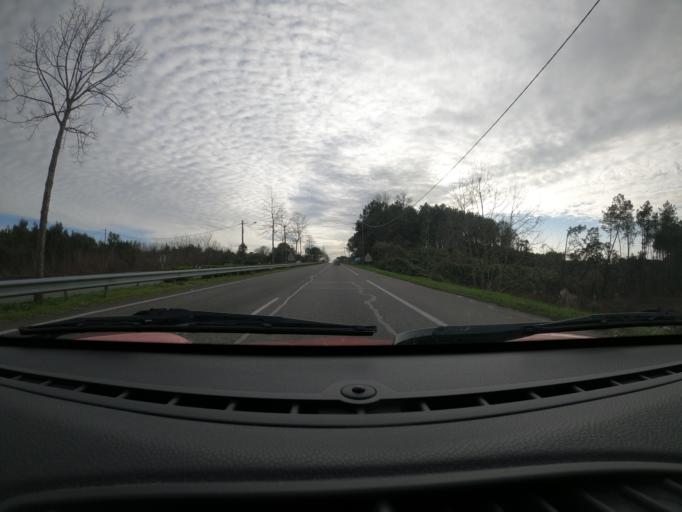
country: FR
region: Aquitaine
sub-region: Departement des Landes
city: Ondres
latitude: 43.5728
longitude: -1.4394
